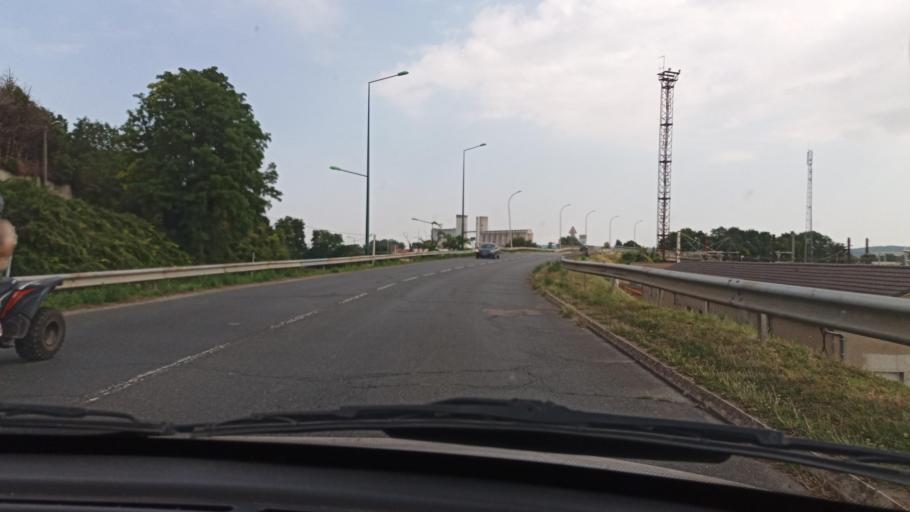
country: FR
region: Bourgogne
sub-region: Departement de l'Yonne
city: Saint-Martin-du-Tertre
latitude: 48.2048
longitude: 3.2646
